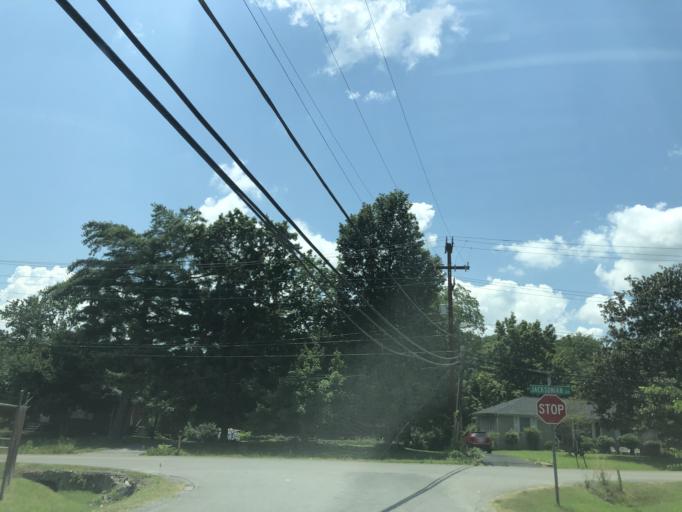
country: US
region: Tennessee
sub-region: Davidson County
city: Lakewood
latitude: 36.1939
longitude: -86.6248
